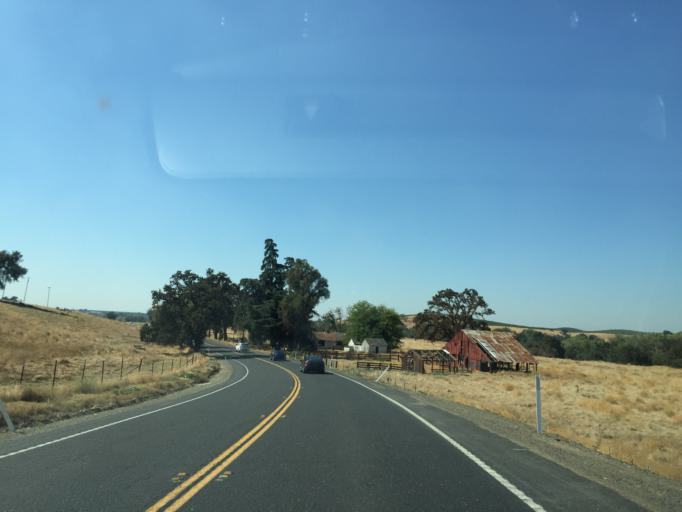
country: US
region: California
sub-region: Stanislaus County
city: East Oakdale
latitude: 37.8067
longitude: -120.7139
